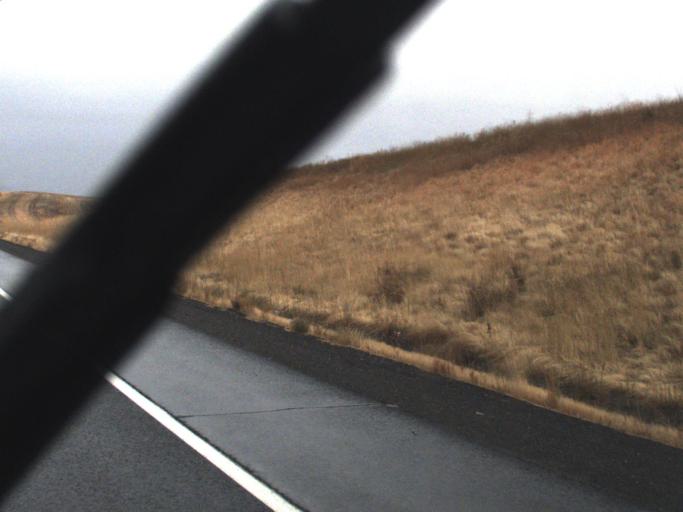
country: US
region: Washington
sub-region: Spokane County
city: Cheney
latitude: 47.3939
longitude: -117.3914
